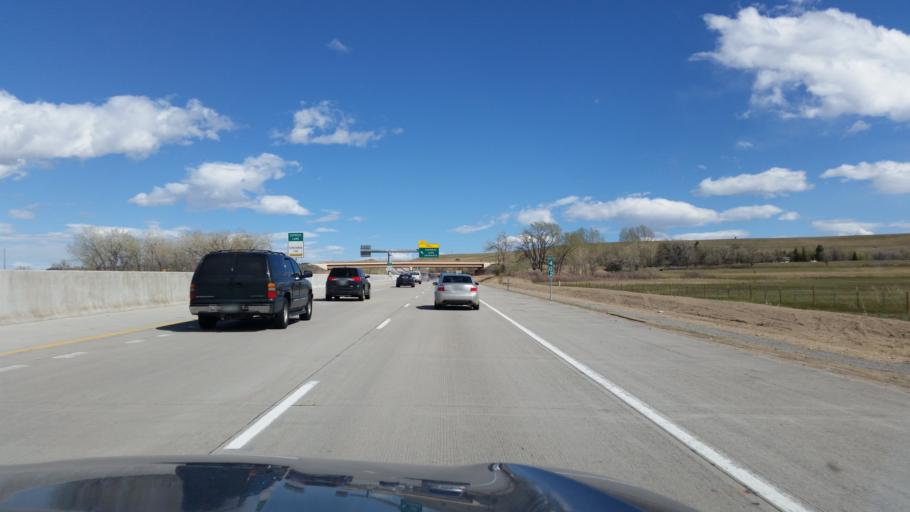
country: US
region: Colorado
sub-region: Boulder County
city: Superior
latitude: 39.9781
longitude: -105.2167
